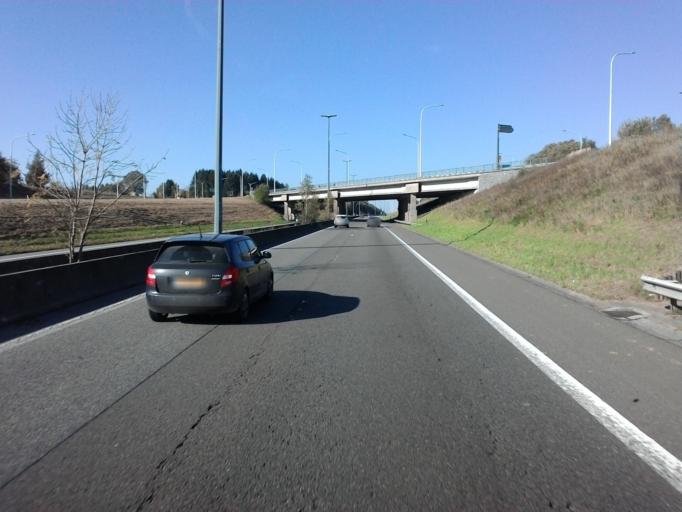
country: BE
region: Wallonia
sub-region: Province du Luxembourg
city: Libin
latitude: 50.0050
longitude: 5.2203
